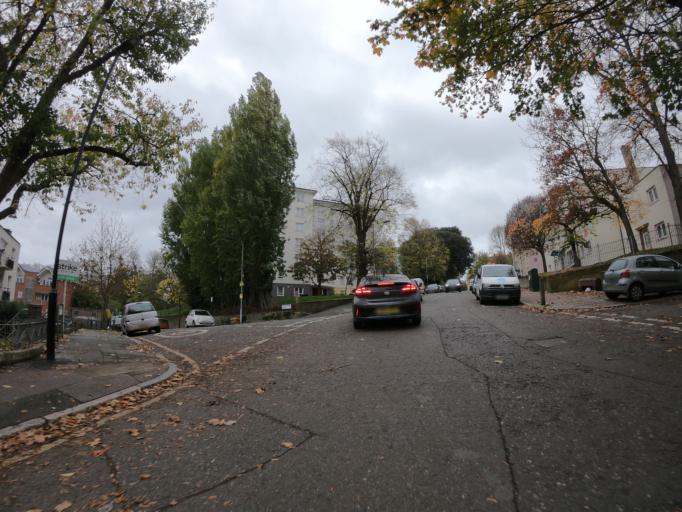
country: GB
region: England
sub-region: Greater London
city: Blackheath
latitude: 51.4811
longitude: 0.0317
